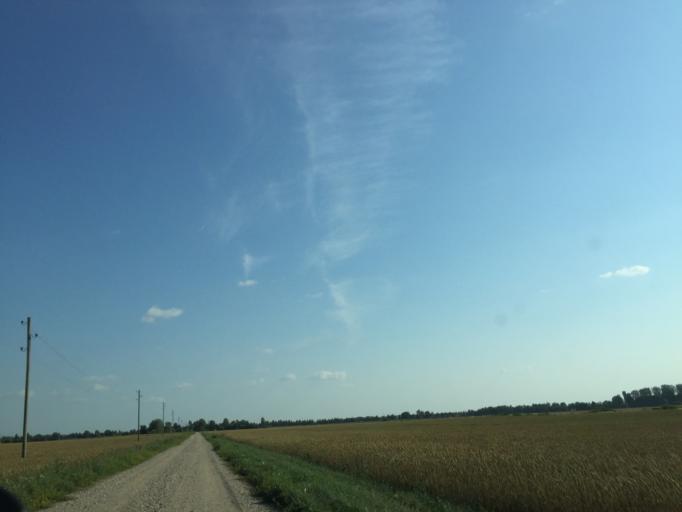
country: LV
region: Jelgava
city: Jelgava
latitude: 56.4621
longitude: 23.6805
